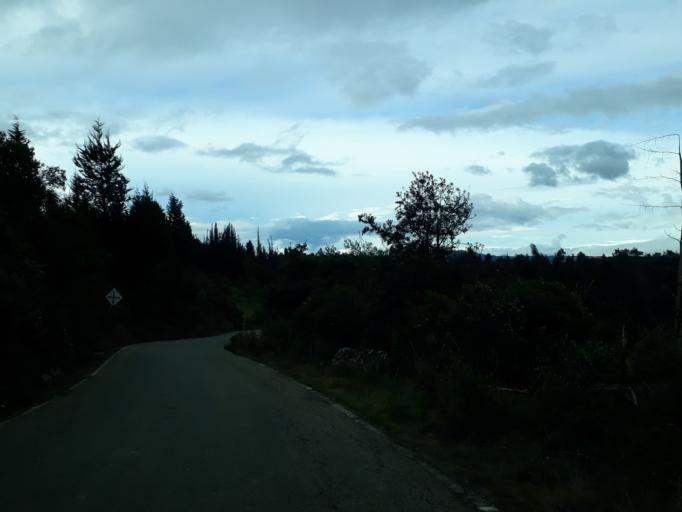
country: CO
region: Cundinamarca
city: Susa
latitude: 5.4014
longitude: -73.7769
